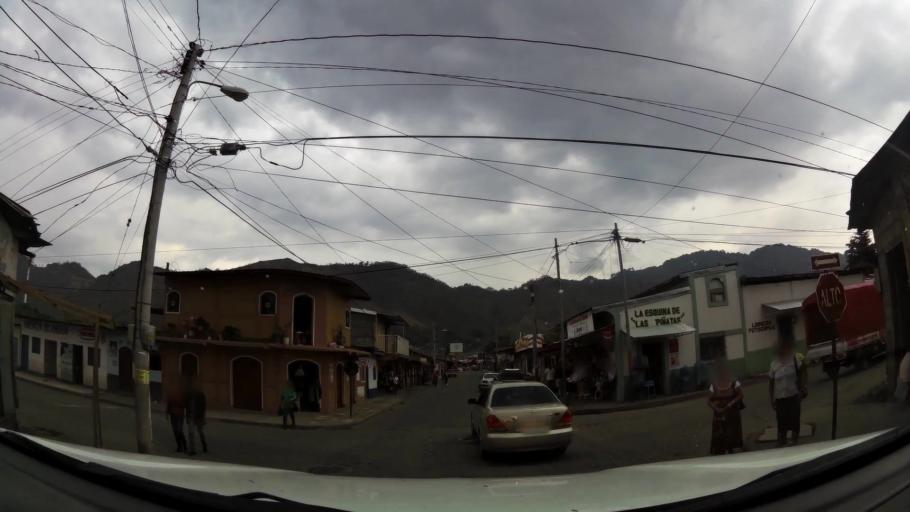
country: NI
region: Jinotega
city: Jinotega
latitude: 13.0932
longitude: -86.0010
